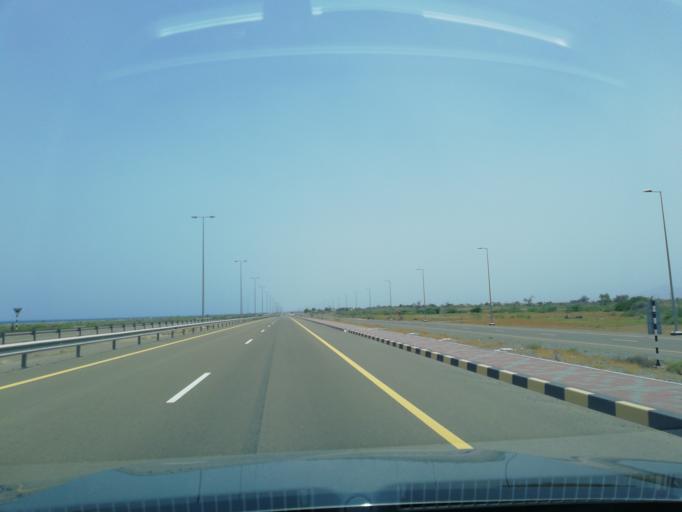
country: OM
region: Al Batinah
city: Shinas
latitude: 24.9054
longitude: 56.3942
